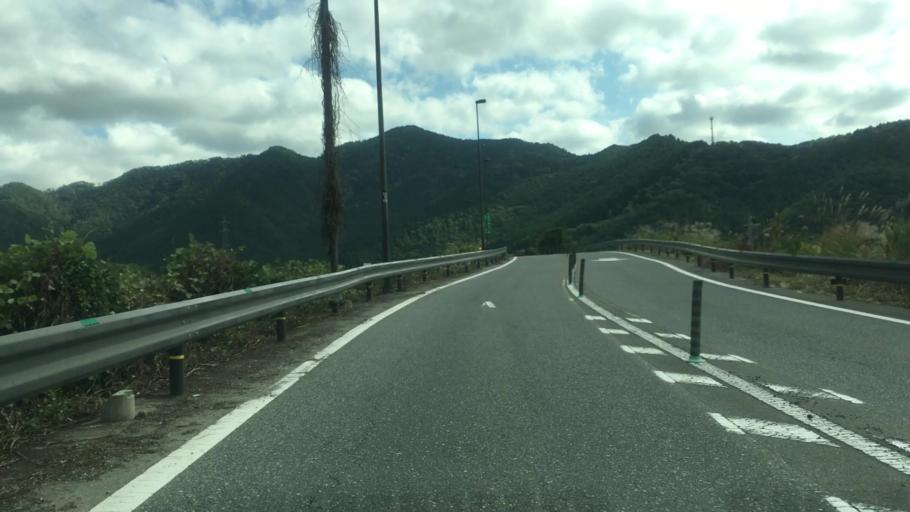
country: JP
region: Kyoto
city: Fukuchiyama
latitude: 35.2431
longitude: 135.0091
